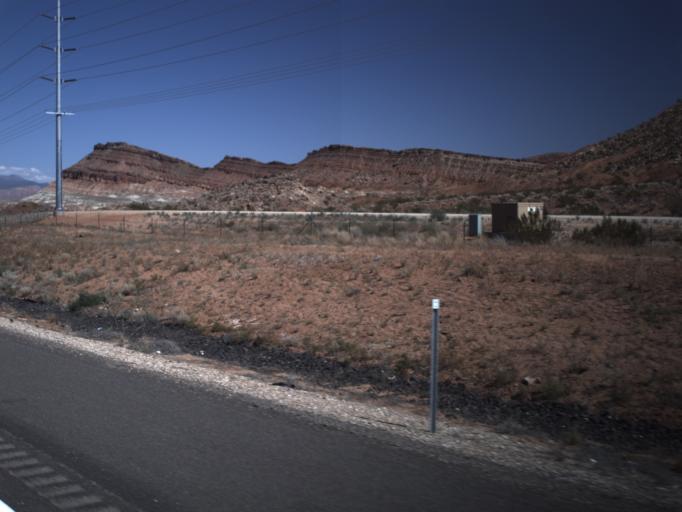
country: US
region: Utah
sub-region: Washington County
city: Washington
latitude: 37.0525
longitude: -113.4857
